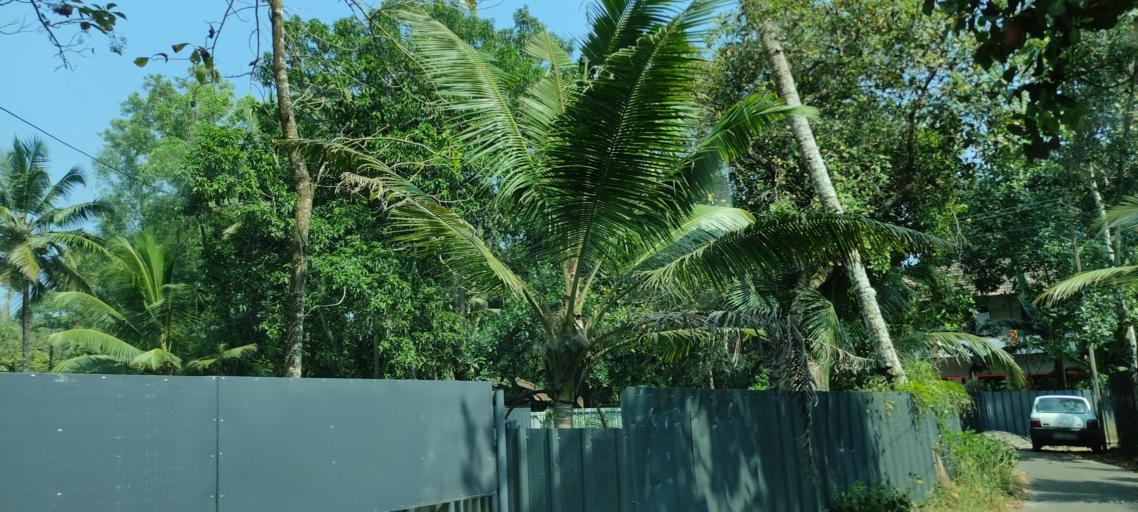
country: IN
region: Kerala
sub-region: Alappuzha
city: Shertallai
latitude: 9.6027
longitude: 76.3200
